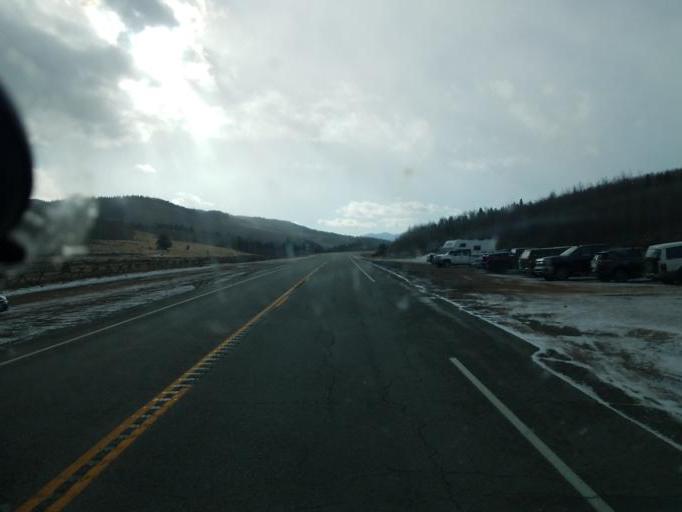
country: US
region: Colorado
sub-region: Summit County
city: Breckenridge
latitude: 39.4133
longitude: -105.7589
